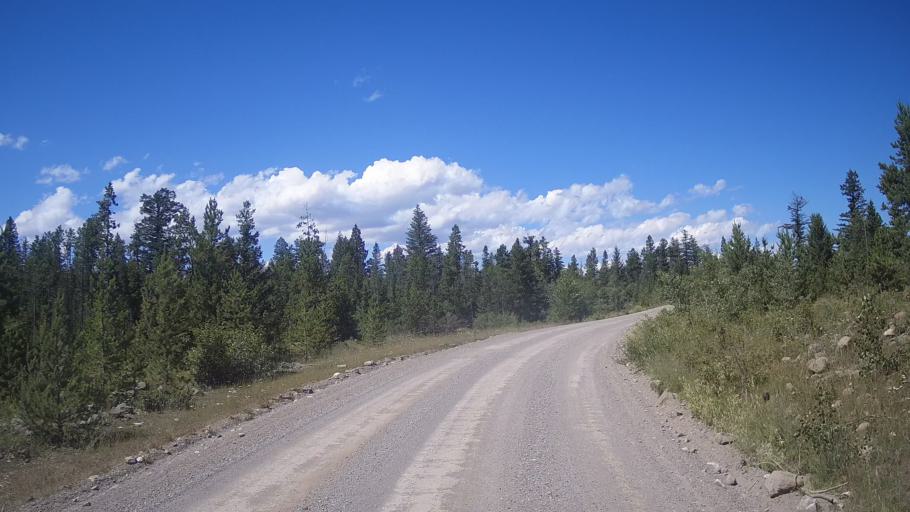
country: CA
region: British Columbia
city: Cache Creek
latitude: 51.1603
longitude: -121.5557
